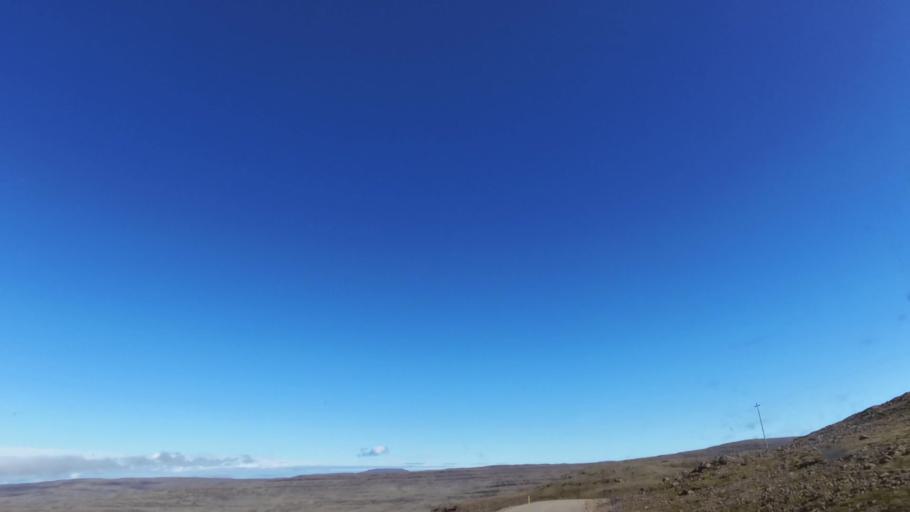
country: IS
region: West
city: Olafsvik
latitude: 65.5555
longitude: -24.2300
